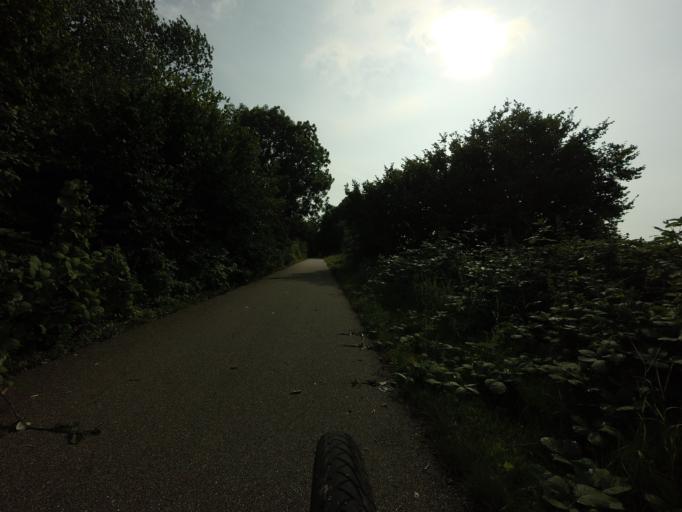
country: DK
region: Zealand
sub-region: Naestved Kommune
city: Fuglebjerg
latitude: 55.2627
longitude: 11.5510
